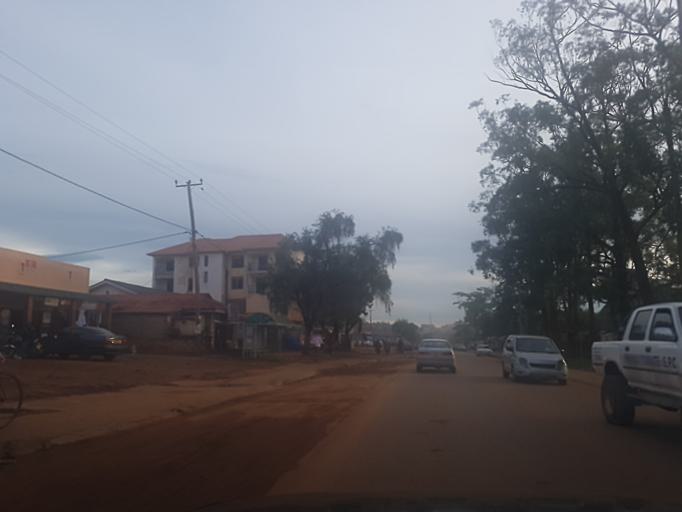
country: UG
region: Central Region
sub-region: Wakiso District
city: Bweyogerere
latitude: 0.3865
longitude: 32.6532
